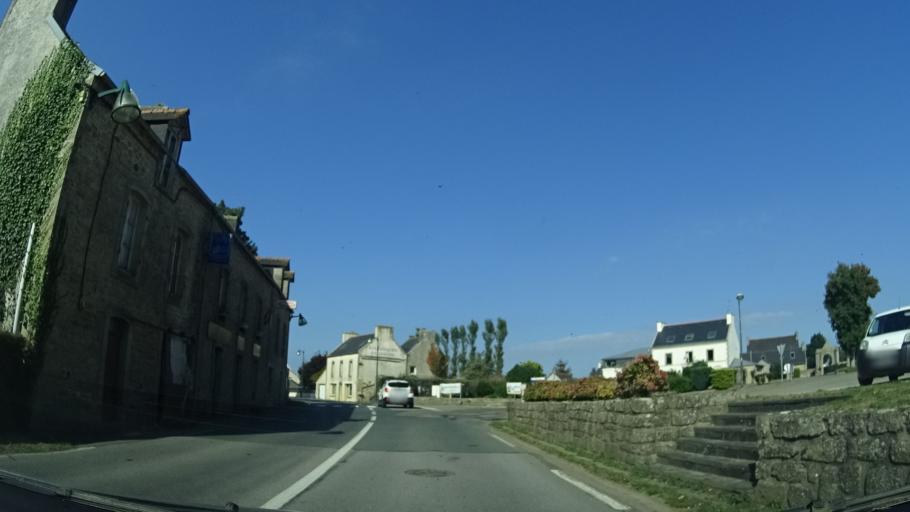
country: FR
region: Brittany
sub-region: Departement du Finistere
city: Douarnenez
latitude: 48.0914
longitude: -4.2732
